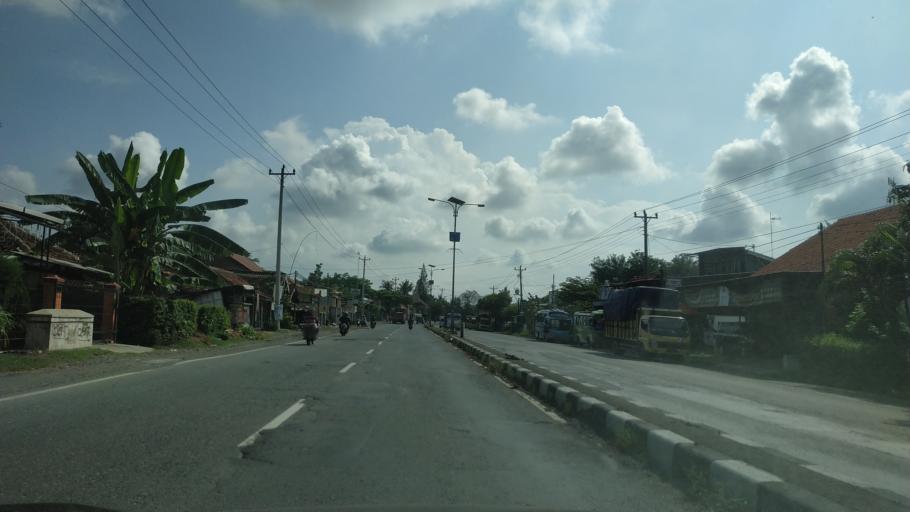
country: ID
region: Central Java
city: Comal
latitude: -6.8914
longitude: 109.5433
